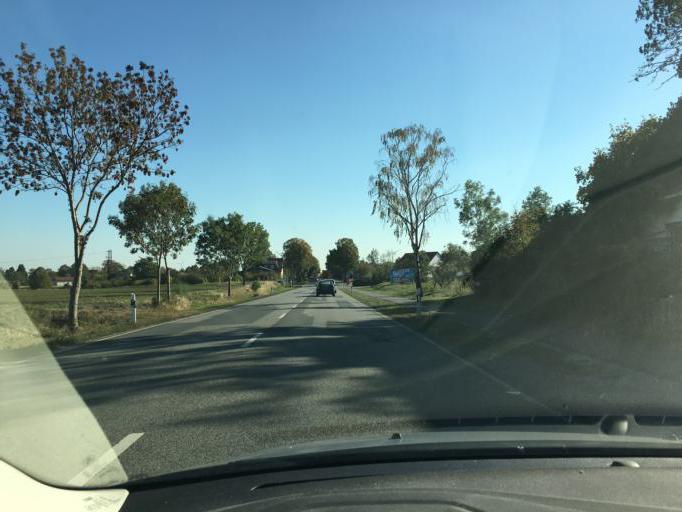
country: DE
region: Saxony-Anhalt
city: Forderstedt
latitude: 51.9051
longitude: 11.6256
